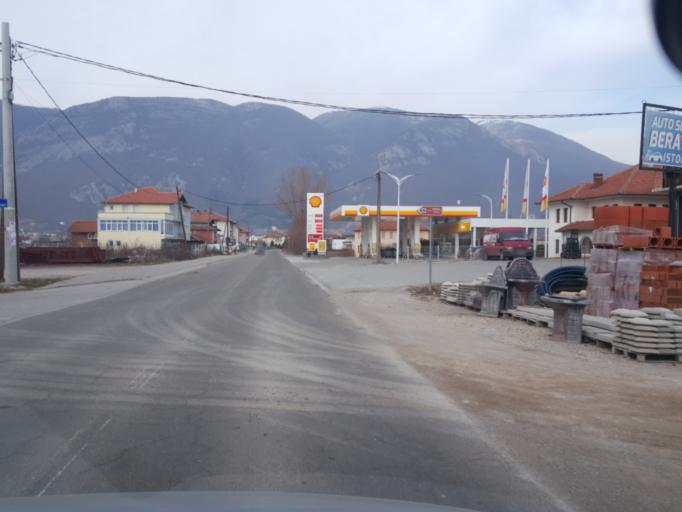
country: XK
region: Pec
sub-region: Komuna e Istogut
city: Istok
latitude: 42.7663
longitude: 20.4876
